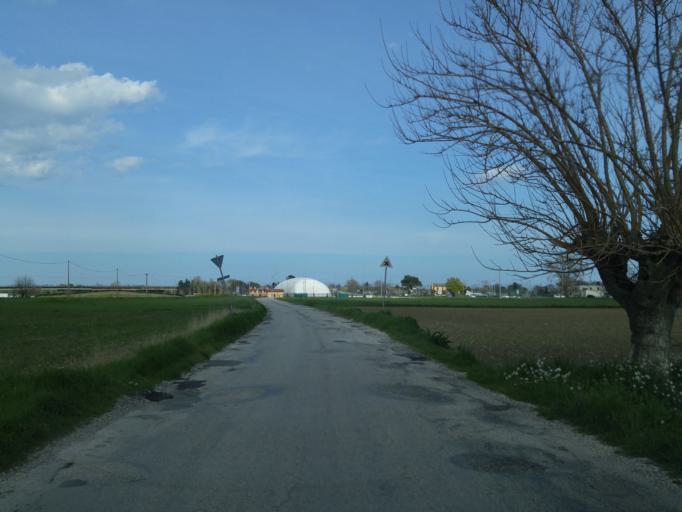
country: IT
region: The Marches
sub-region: Provincia di Pesaro e Urbino
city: Rosciano
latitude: 43.8095
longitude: 13.0112
